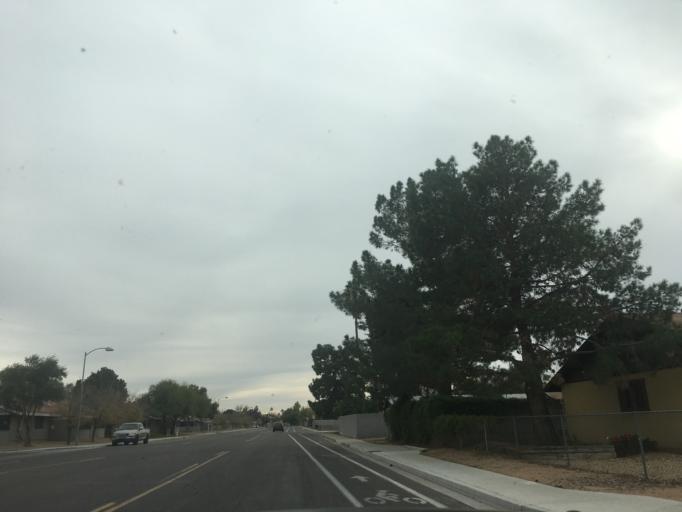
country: US
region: Arizona
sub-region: Maricopa County
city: Gilbert
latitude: 33.3536
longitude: -111.7819
